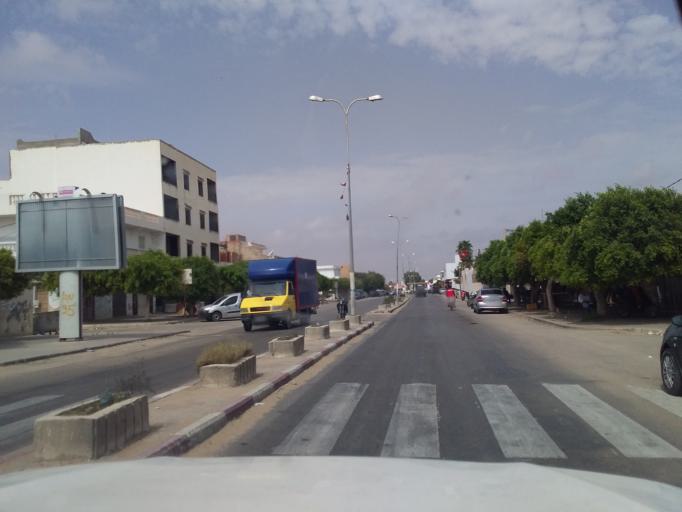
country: TN
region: Qabis
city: Matmata
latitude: 33.6146
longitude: 10.2908
